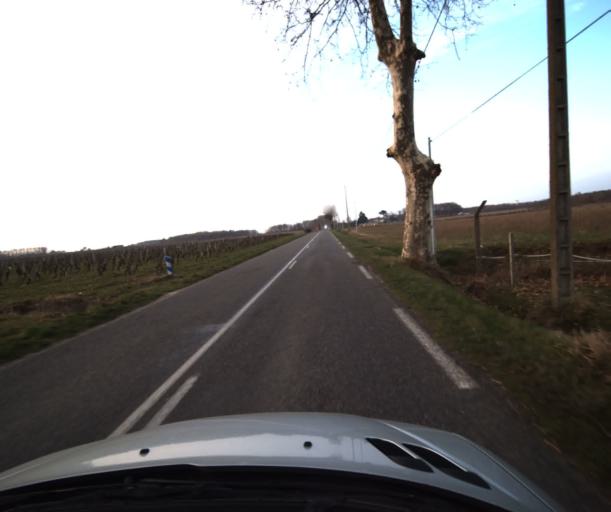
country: FR
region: Midi-Pyrenees
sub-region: Departement de la Haute-Garonne
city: Fronton
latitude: 43.8739
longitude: 1.3791
